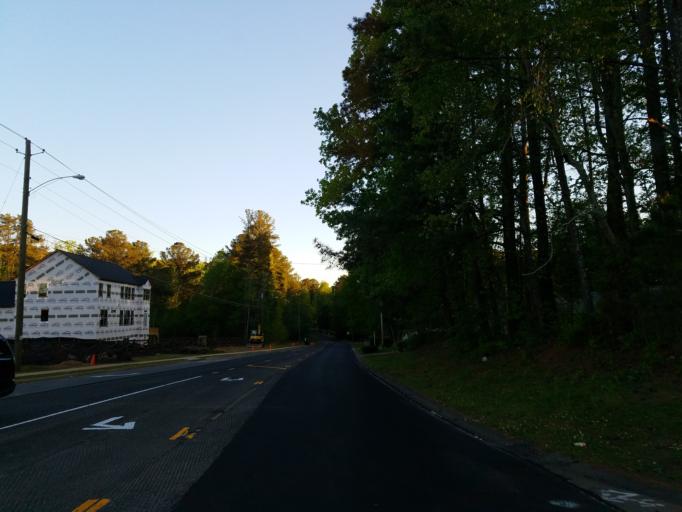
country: US
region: Georgia
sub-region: Cobb County
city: Powder Springs
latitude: 33.8979
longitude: -84.6241
